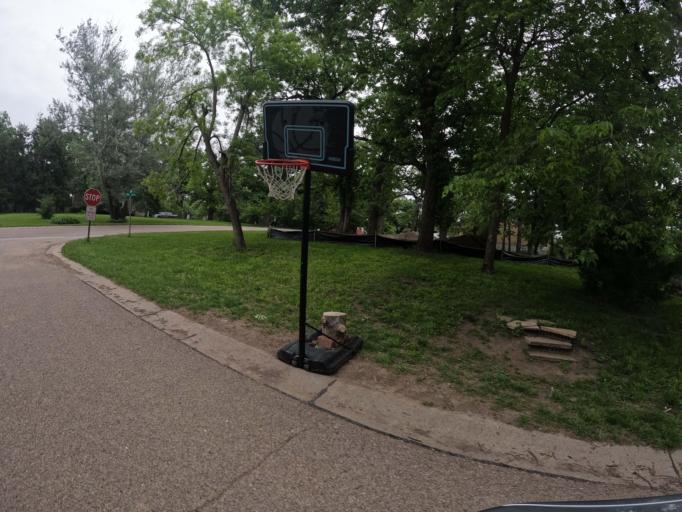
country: US
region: Nebraska
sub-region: Sarpy County
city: Offutt Air Force Base
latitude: 41.0498
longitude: -95.9691
